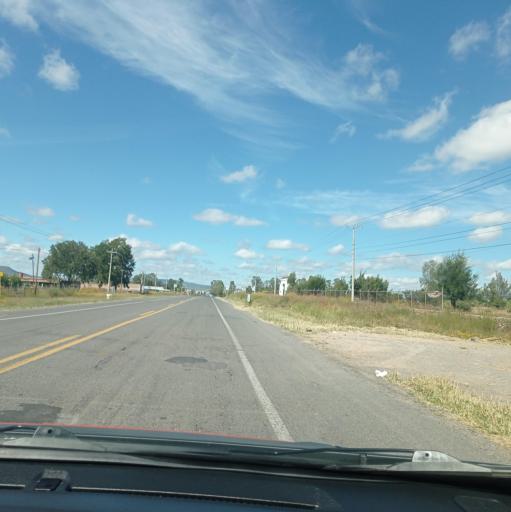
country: MX
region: Jalisco
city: San Miguel el Alto
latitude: 21.0195
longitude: -102.3451
